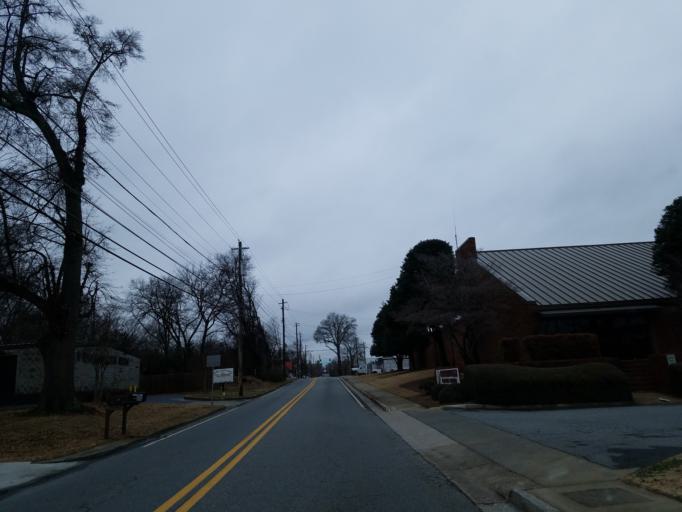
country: US
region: Georgia
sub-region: Bartow County
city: Cartersville
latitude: 34.1603
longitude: -84.7949
